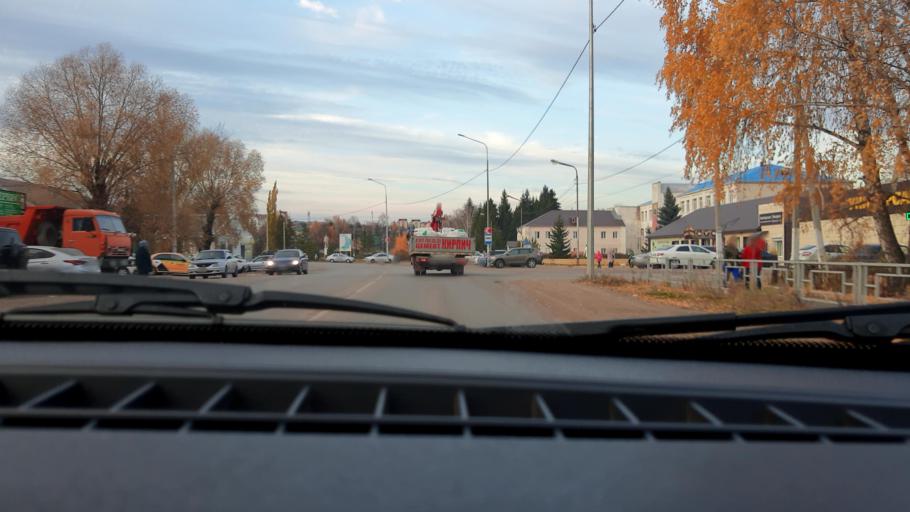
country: RU
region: Bashkortostan
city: Mikhaylovka
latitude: 54.8023
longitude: 55.8923
